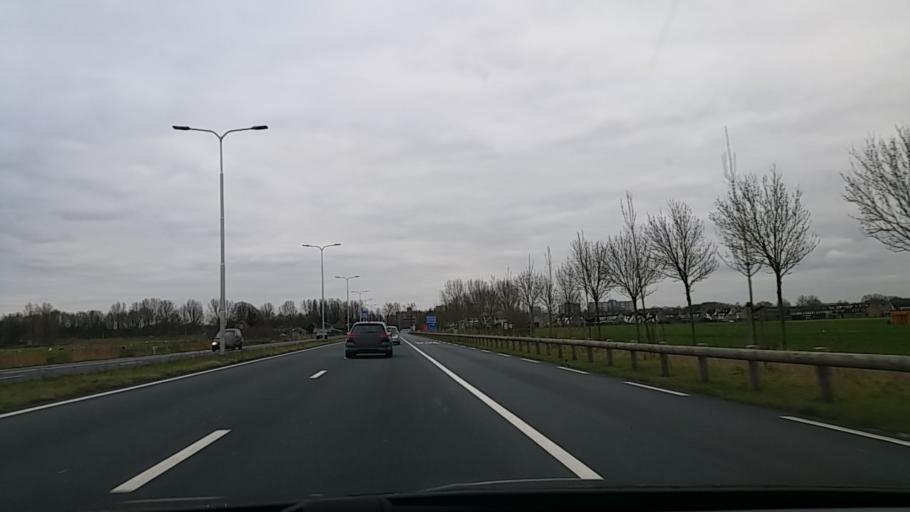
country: NL
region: South Holland
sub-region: Gemeente Alphen aan den Rijn
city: Alphen aan den Rijn
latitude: 52.1603
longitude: 4.6656
